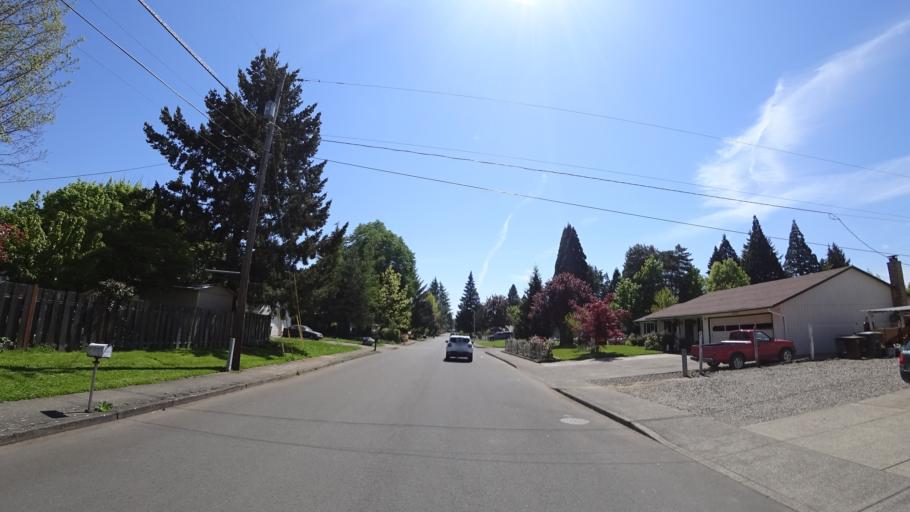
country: US
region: Oregon
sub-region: Washington County
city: Hillsboro
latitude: 45.5145
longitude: -122.9641
